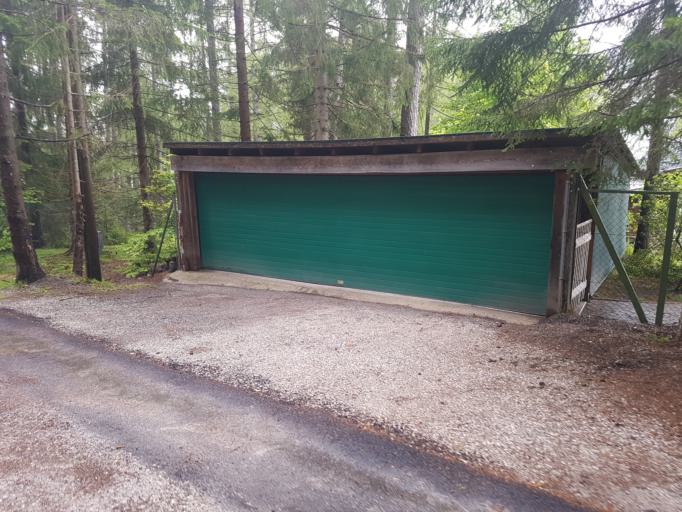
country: AT
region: Tyrol
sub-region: Politischer Bezirk Imst
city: Obsteig
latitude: 47.3042
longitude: 10.9218
